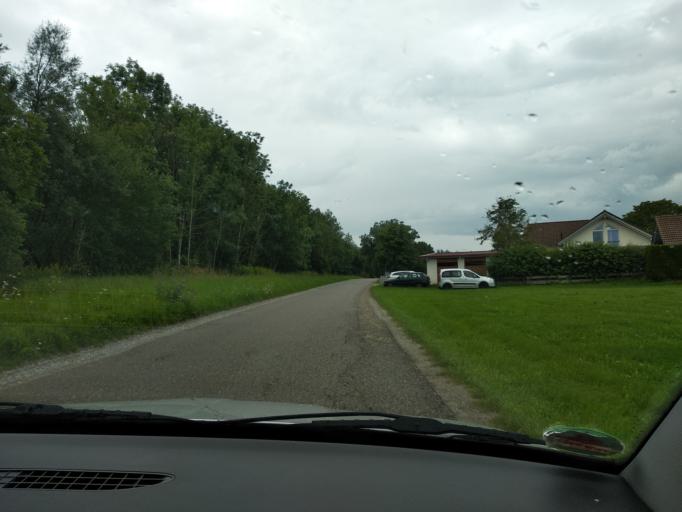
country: DE
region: Baden-Wuerttemberg
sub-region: Tuebingen Region
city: Leutkirch im Allgau
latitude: 47.8550
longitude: 9.9993
